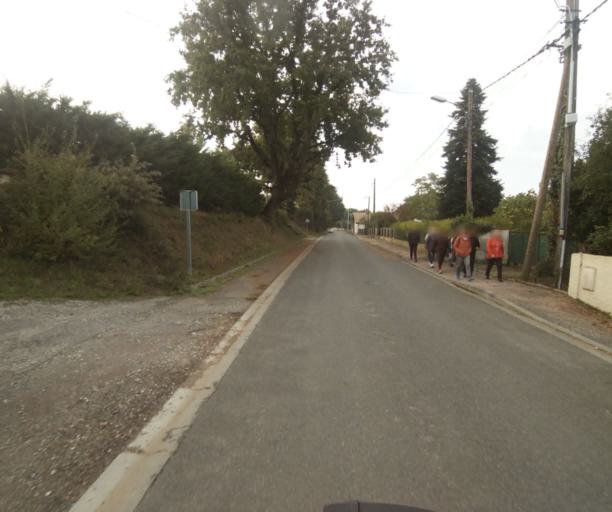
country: FR
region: Midi-Pyrenees
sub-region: Departement du Tarn-et-Garonne
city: Montech
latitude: 43.9649
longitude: 1.2261
